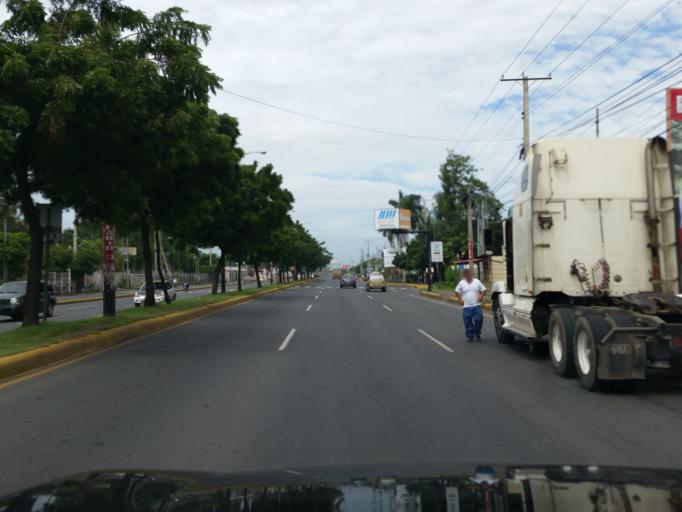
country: NI
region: Managua
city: Managua
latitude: 12.1503
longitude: -86.2193
